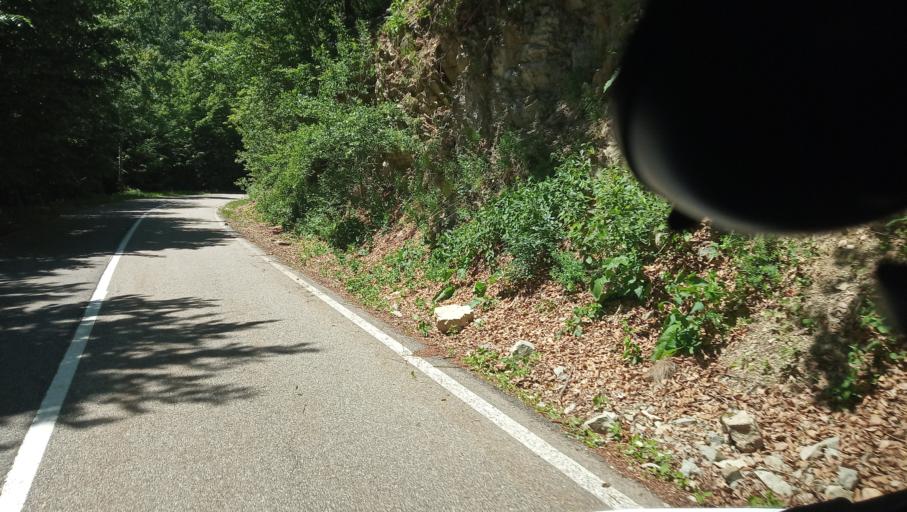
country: RO
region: Mehedinti
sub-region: Comuna Obarsia-Closani
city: Obarsia-Closani
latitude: 45.0552
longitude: 22.6232
